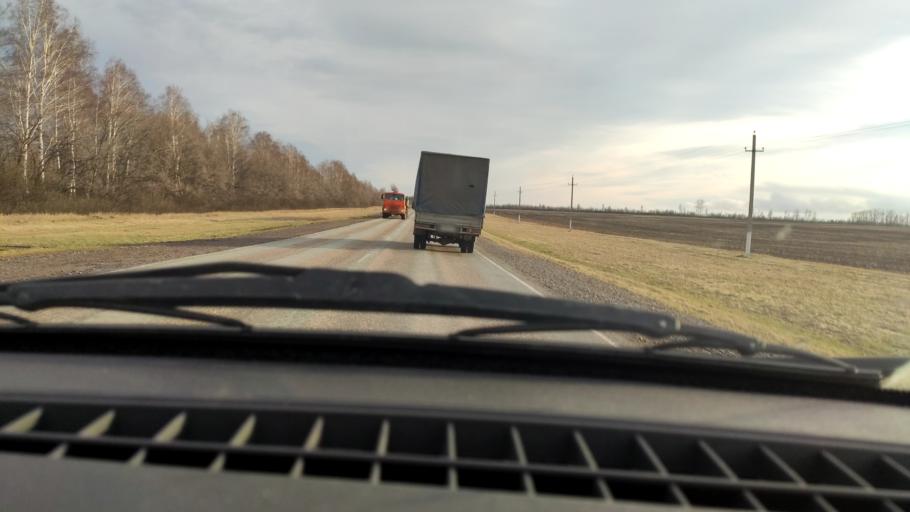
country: RU
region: Bashkortostan
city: Davlekanovo
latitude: 54.3364
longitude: 55.1698
